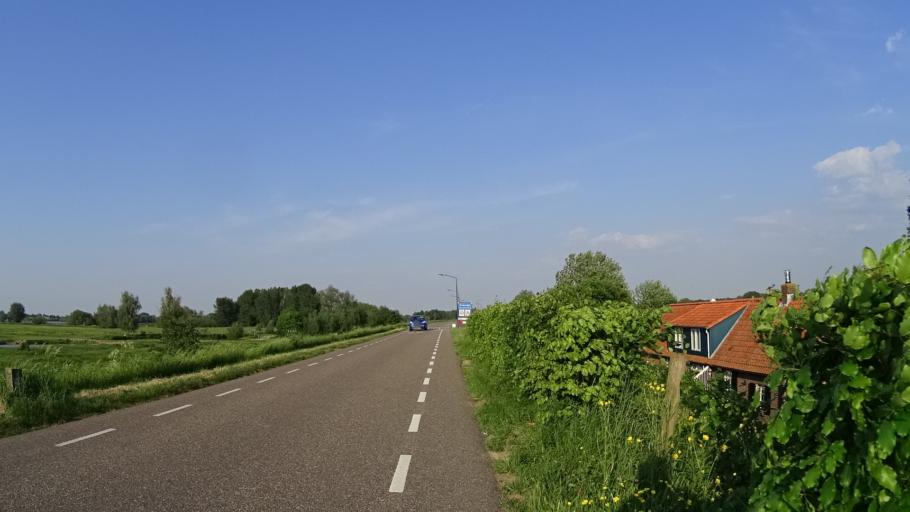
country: NL
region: South Holland
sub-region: Gemeente Gorinchem
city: Gorinchem
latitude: 51.8157
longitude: 4.9782
